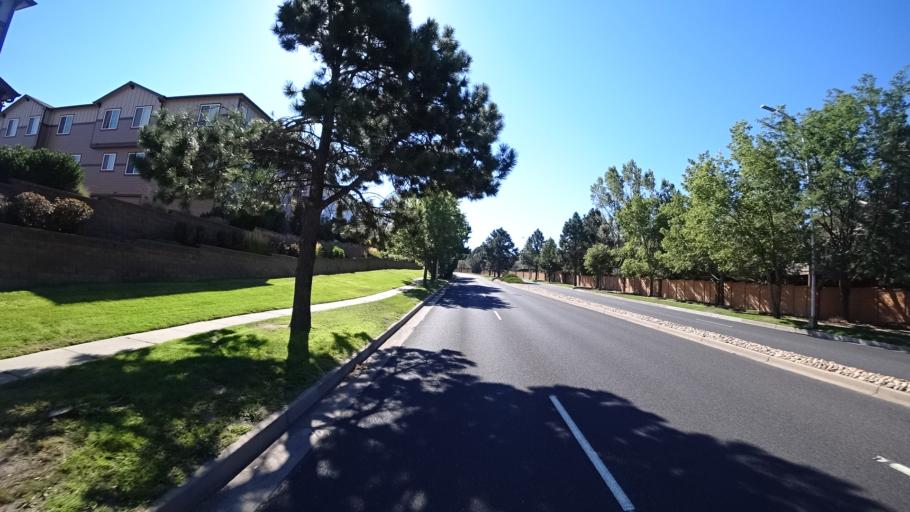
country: US
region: Colorado
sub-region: El Paso County
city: Cimarron Hills
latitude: 38.9210
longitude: -104.7414
